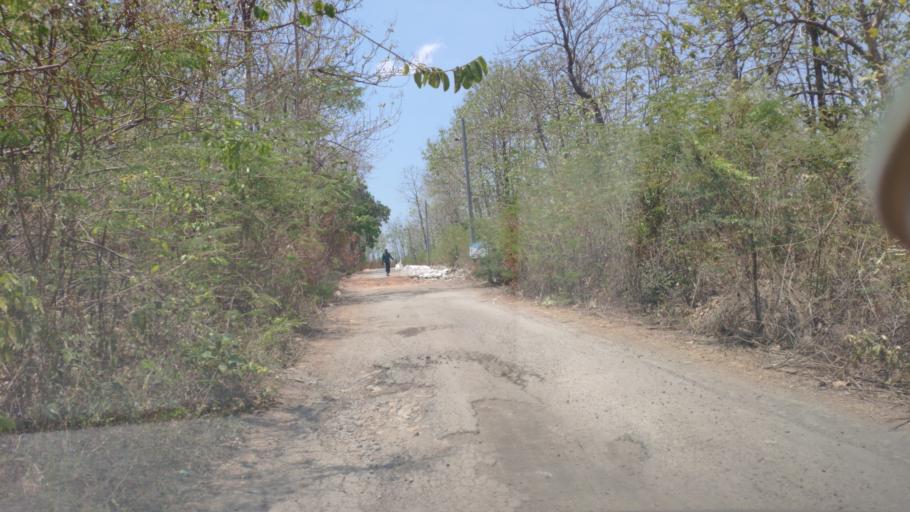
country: ID
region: Central Java
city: Randublatung
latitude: -7.2658
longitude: 111.3789
